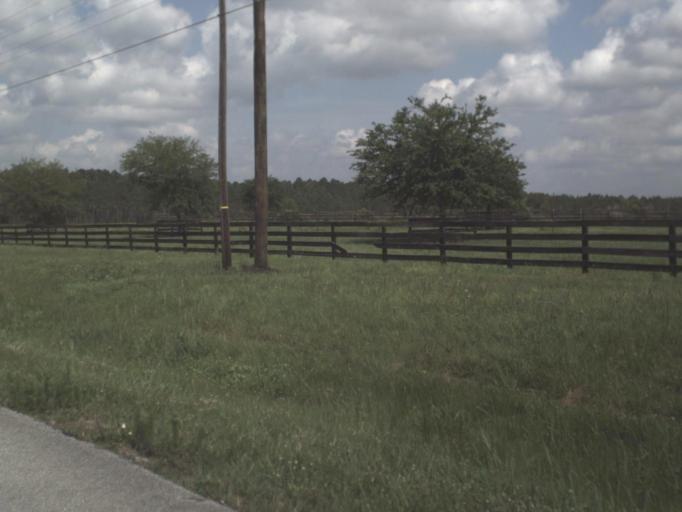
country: US
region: Florida
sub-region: Saint Johns County
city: Saint Augustine Shores
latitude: 29.7258
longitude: -81.4466
